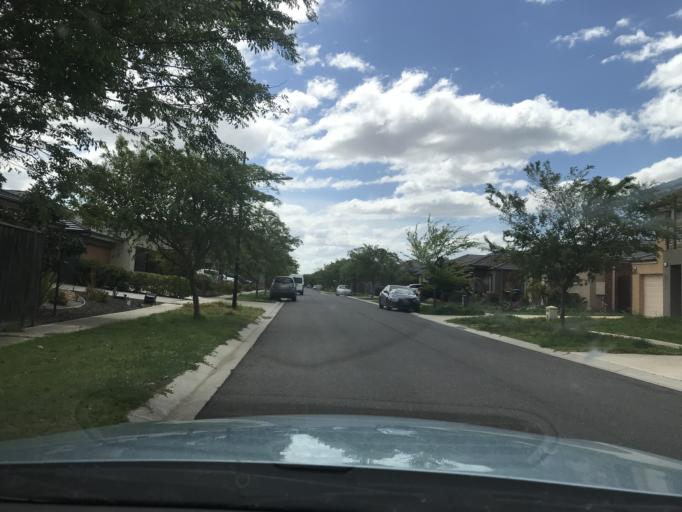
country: AU
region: Victoria
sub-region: Wyndham
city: Williams Landing
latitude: -37.8606
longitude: 144.7469
